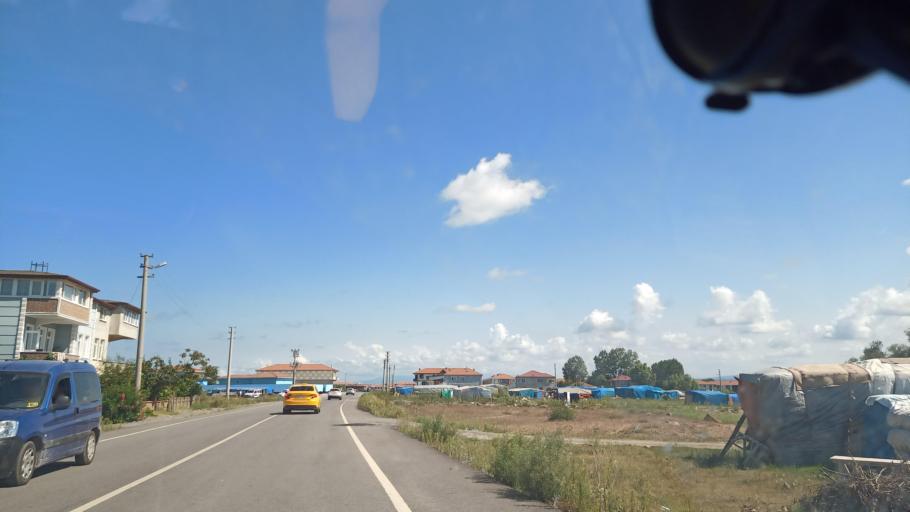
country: TR
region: Sakarya
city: Karasu
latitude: 41.1173
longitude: 30.6635
